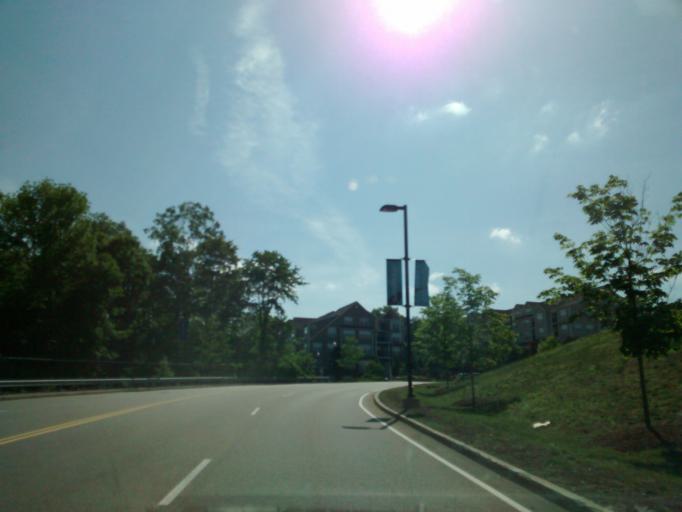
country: US
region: Massachusetts
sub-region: Worcester County
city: Shrewsbury
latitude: 42.2870
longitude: -71.6714
